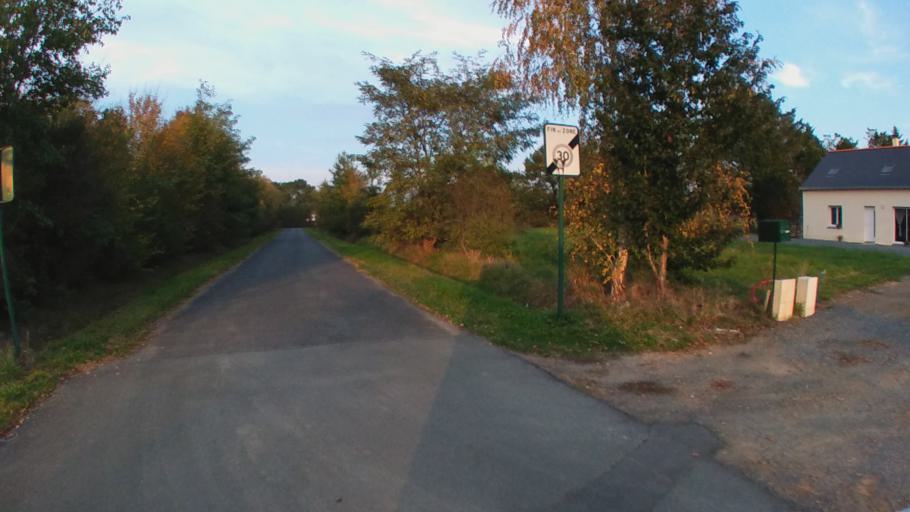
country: FR
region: Pays de la Loire
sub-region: Departement de Maine-et-Loire
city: Vivy
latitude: 47.3283
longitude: -0.0499
